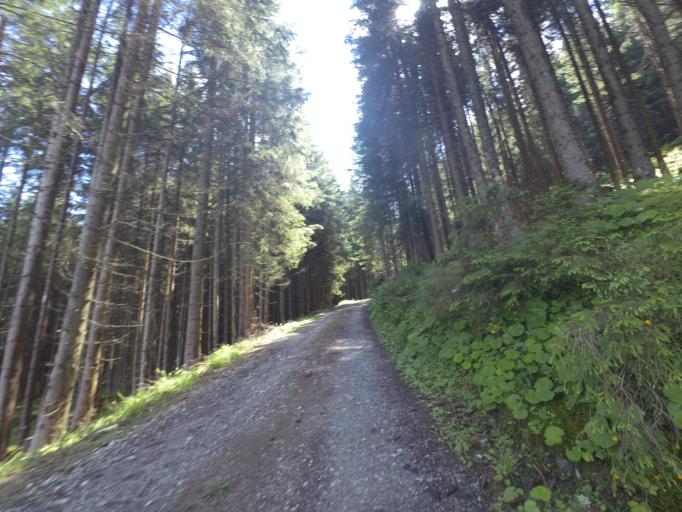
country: AT
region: Salzburg
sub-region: Politischer Bezirk Sankt Johann im Pongau
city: Schwarzach im Pongau
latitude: 47.3051
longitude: 13.1558
